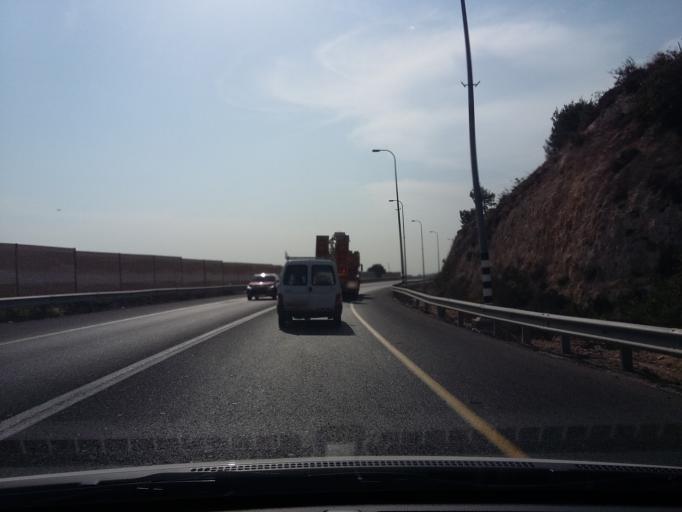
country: PS
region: West Bank
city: Al Khadir
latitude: 31.6929
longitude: 35.1608
